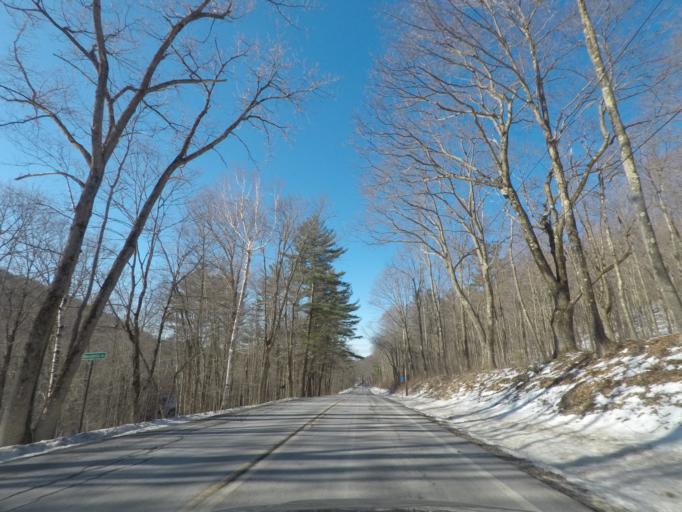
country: US
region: Massachusetts
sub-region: Berkshire County
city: West Stockbridge
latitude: 42.3417
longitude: -73.4738
